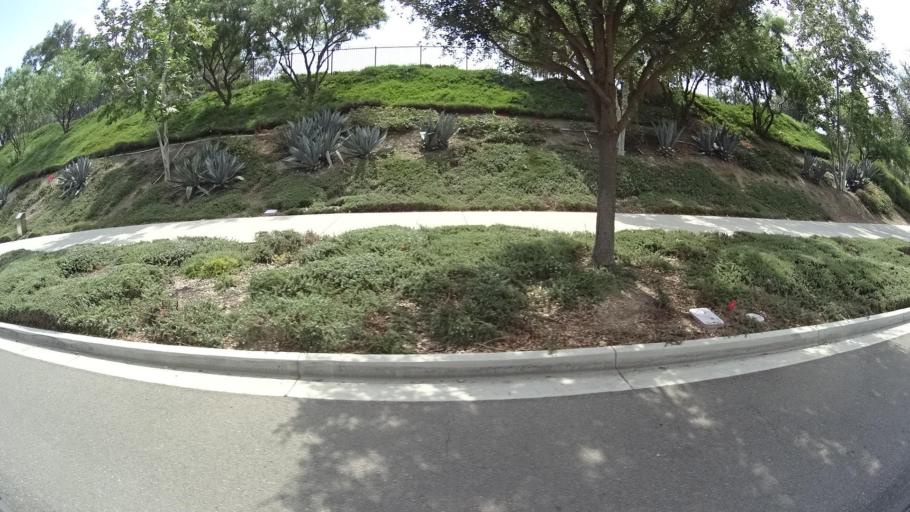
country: US
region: California
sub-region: Orange County
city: San Juan Capistrano
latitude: 33.5222
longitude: -117.6274
